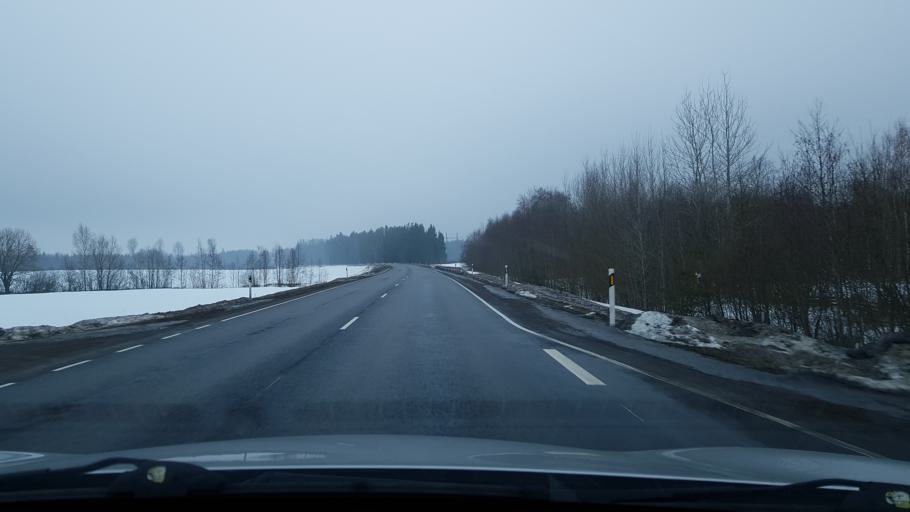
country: EE
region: Valgamaa
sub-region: Valga linn
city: Valga
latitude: 57.8977
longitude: 26.1676
